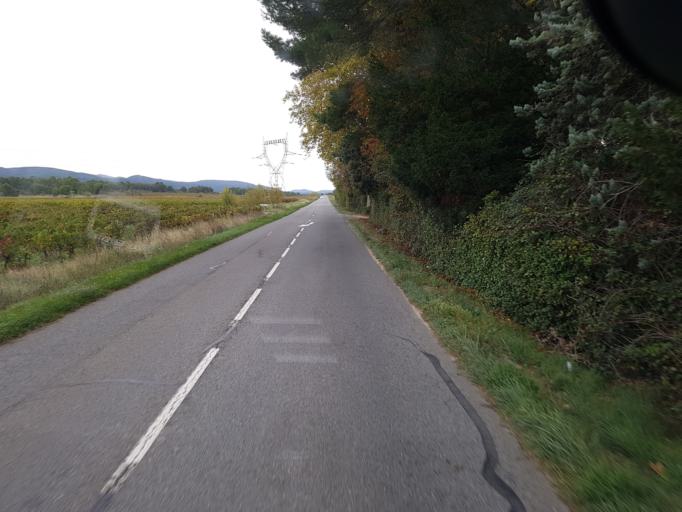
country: FR
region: Languedoc-Roussillon
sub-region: Departement de l'Aude
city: Laure-Minervois
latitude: 43.3017
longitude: 2.4688
